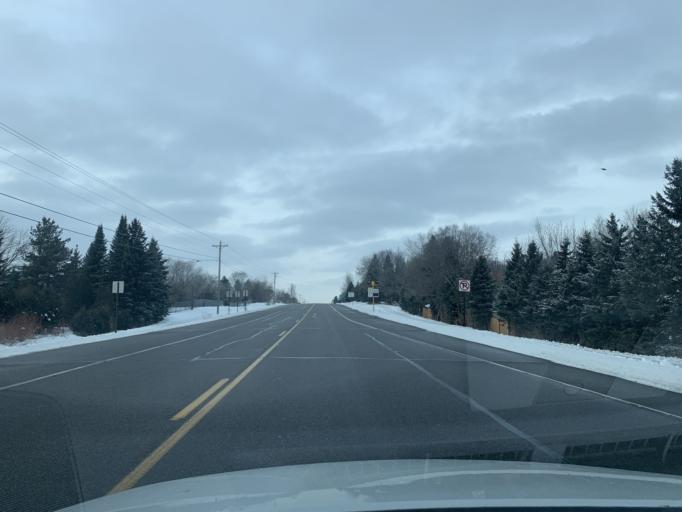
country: US
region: Minnesota
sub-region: Anoka County
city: Ramsey
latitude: 45.2407
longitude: -93.4103
